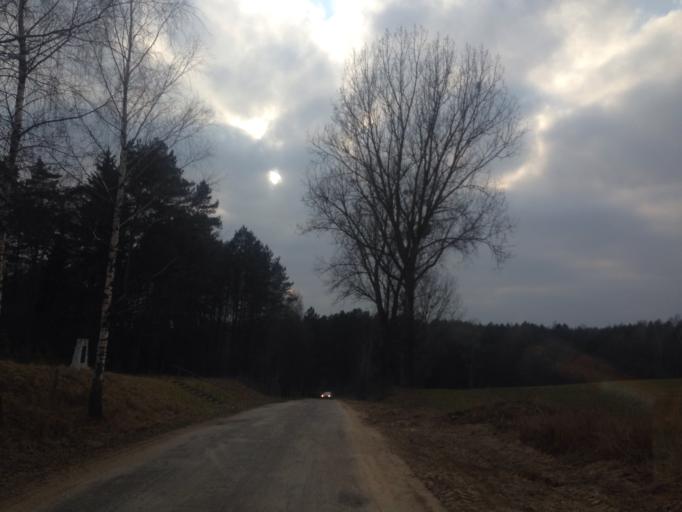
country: PL
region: Warmian-Masurian Voivodeship
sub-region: Powiat dzialdowski
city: Lidzbark
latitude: 53.3472
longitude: 19.7405
